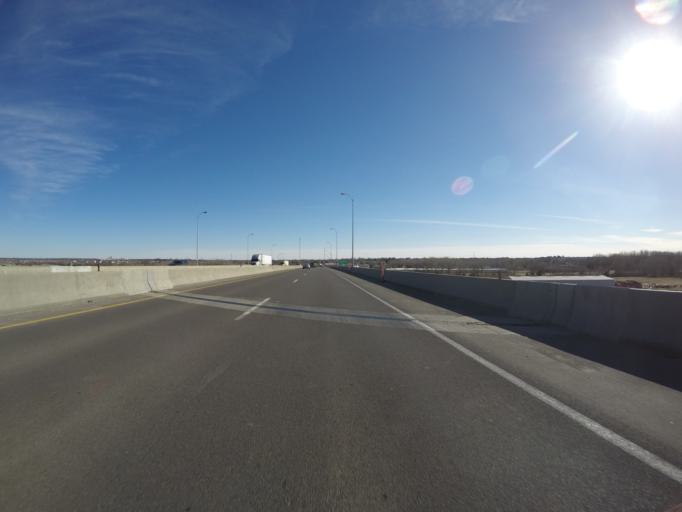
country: US
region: Nebraska
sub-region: Lancaster County
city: Lincoln
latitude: 40.8073
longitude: -96.7515
